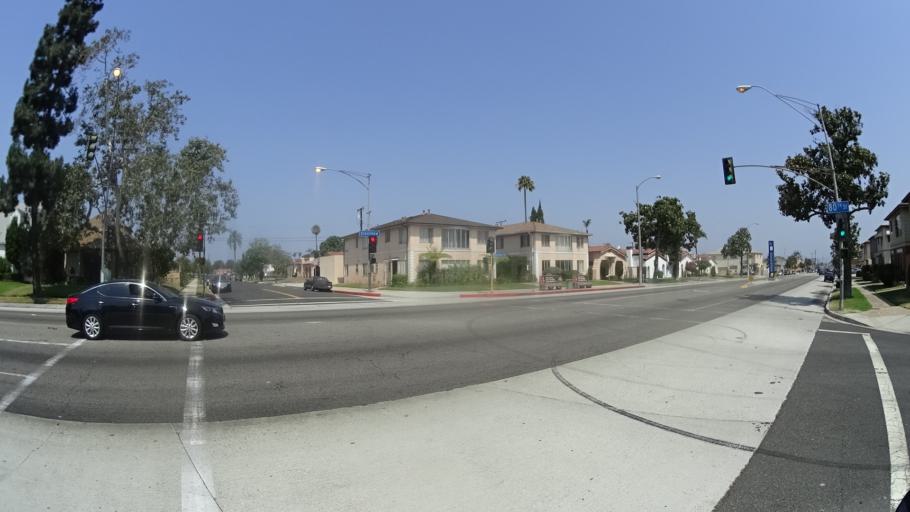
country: US
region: California
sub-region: Los Angeles County
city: Inglewood
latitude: 33.9662
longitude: -118.3308
